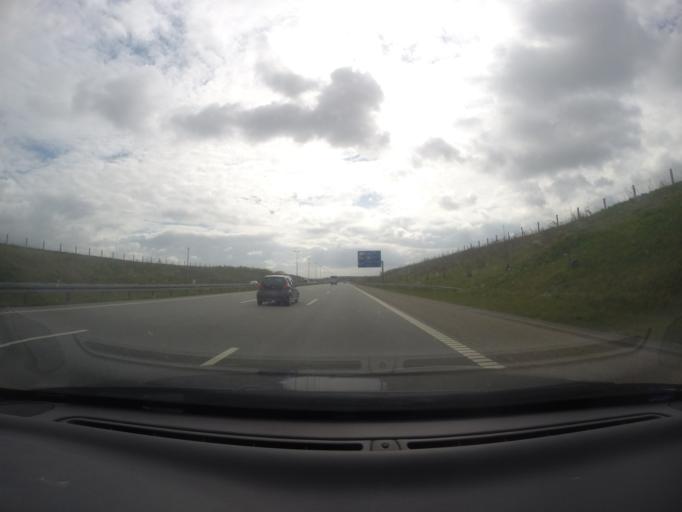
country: DK
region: Capital Region
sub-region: Glostrup Kommune
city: Glostrup
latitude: 55.6964
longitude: 12.3900
